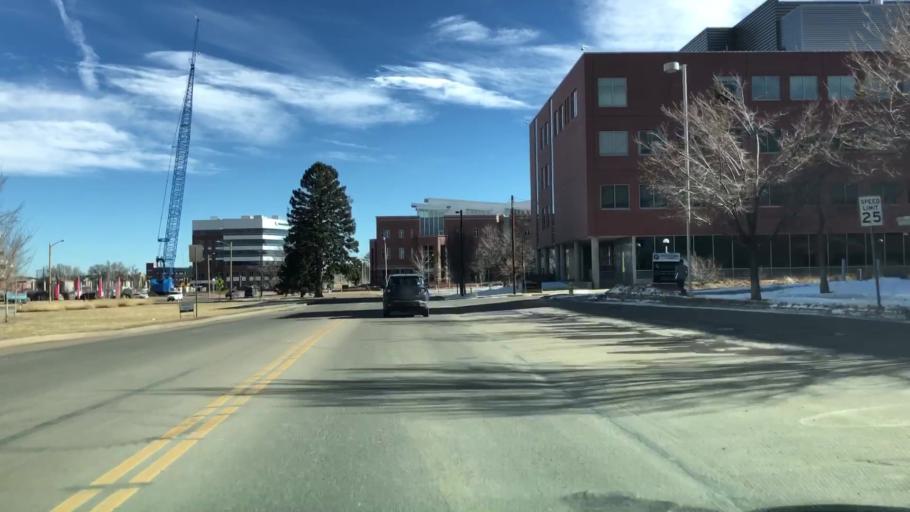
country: US
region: Colorado
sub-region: Adams County
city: Aurora
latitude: 39.7473
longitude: -104.8393
